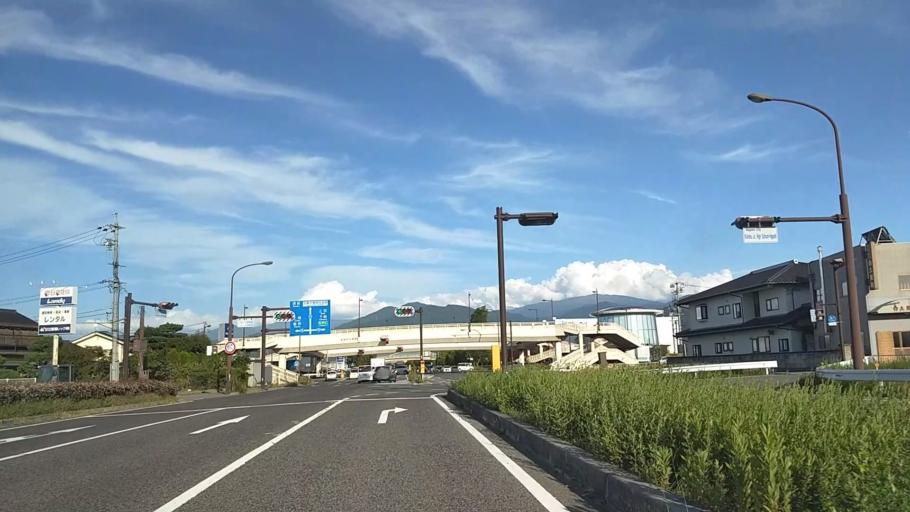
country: JP
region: Nagano
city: Nagano-shi
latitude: 36.6054
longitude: 138.1934
